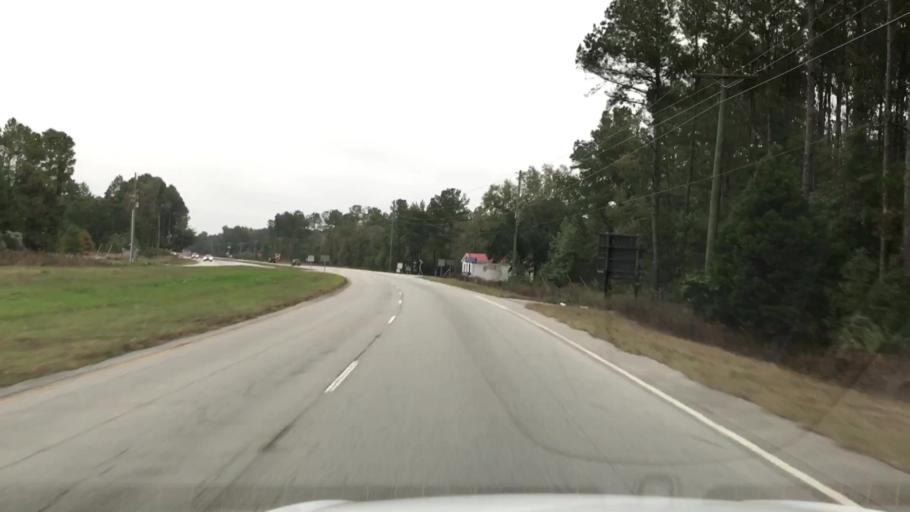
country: US
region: South Carolina
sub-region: Charleston County
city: Awendaw
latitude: 32.9893
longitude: -79.6465
